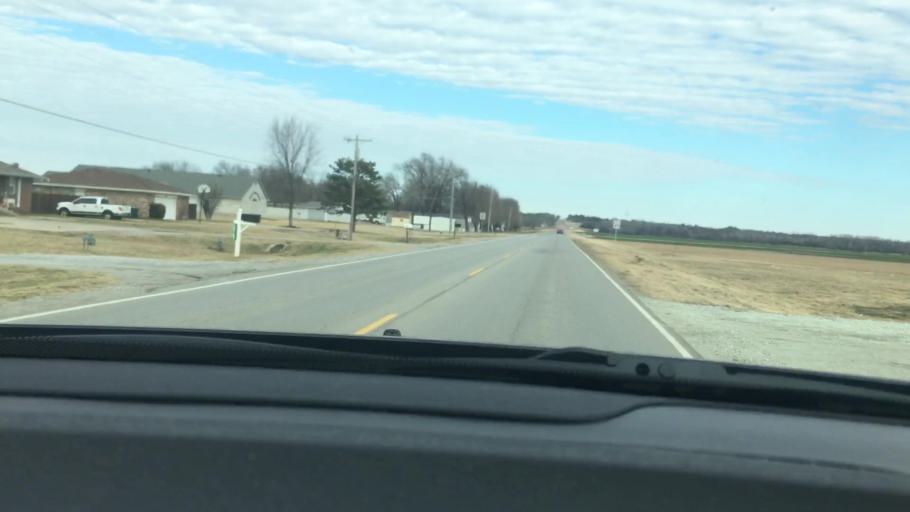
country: US
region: Oklahoma
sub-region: Garvin County
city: Pauls Valley
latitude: 34.7500
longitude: -97.2094
